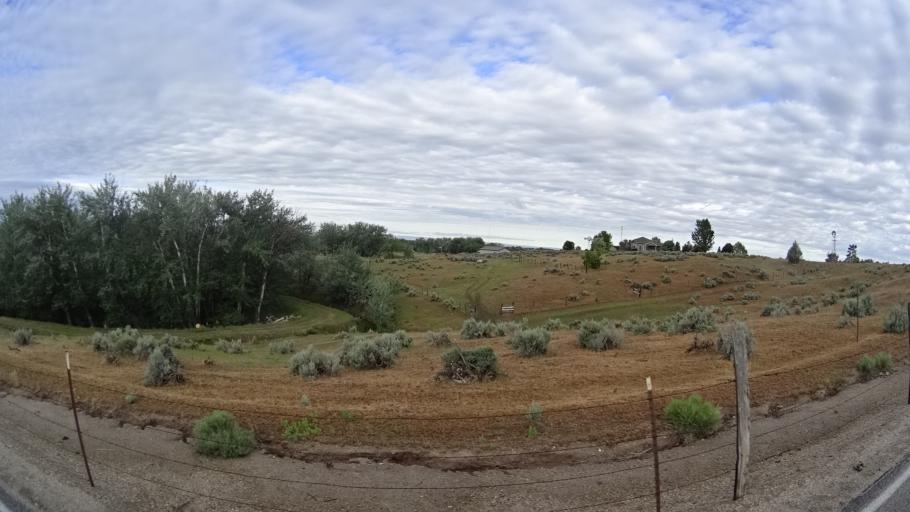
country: US
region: Idaho
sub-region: Ada County
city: Star
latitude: 43.7217
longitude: -116.5132
